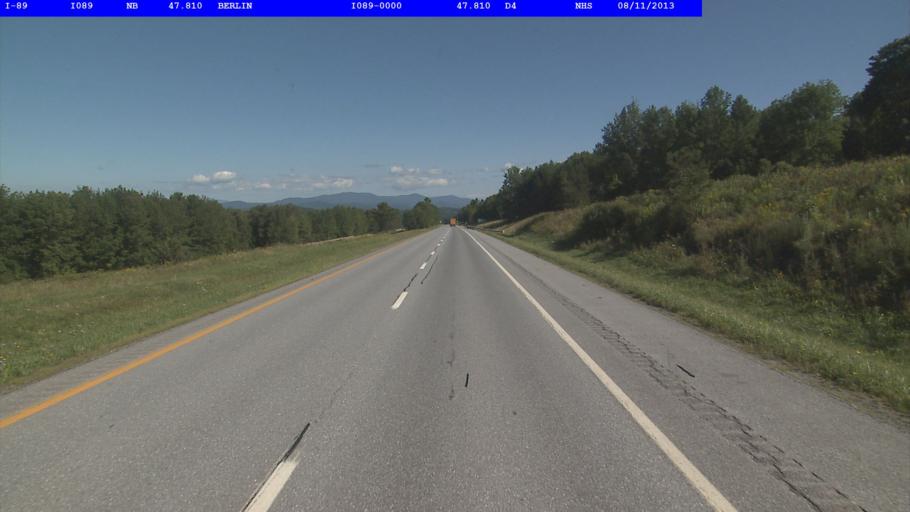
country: US
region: Vermont
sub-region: Orange County
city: Williamstown
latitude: 44.1805
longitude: -72.5756
